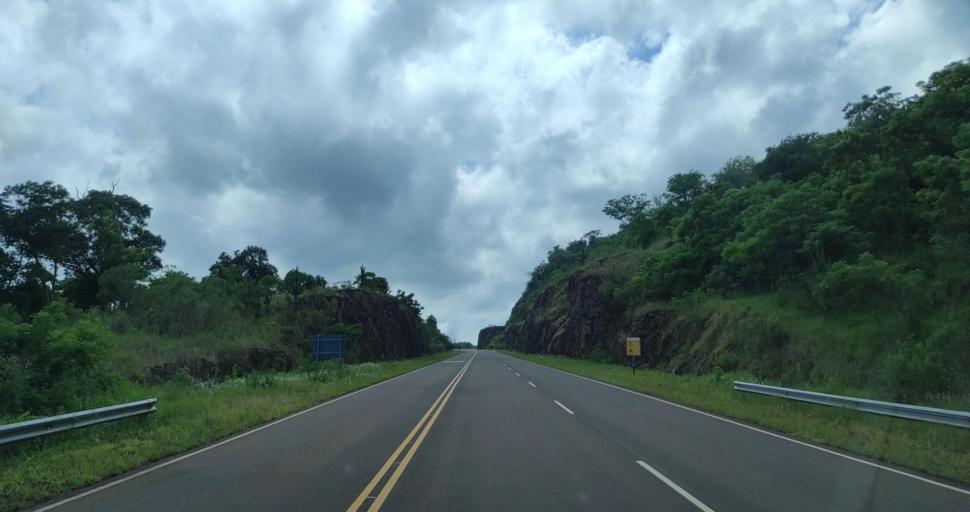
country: AR
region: Misiones
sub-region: Departamento de Veinticinco de Mayo
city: Veinticinco de Mayo
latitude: -27.3841
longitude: -54.8141
